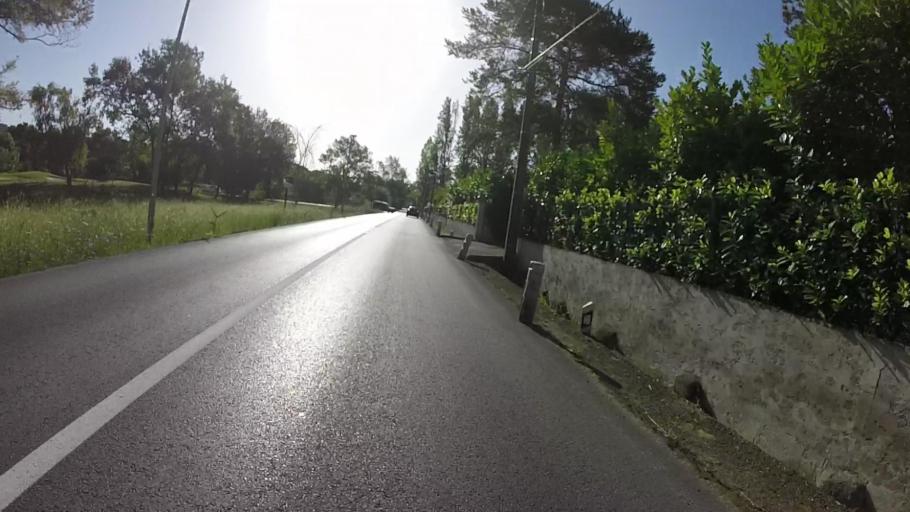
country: FR
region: Provence-Alpes-Cote d'Azur
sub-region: Departement des Alpes-Maritimes
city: Chateauneuf-Grasse
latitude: 43.6575
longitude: 6.9849
